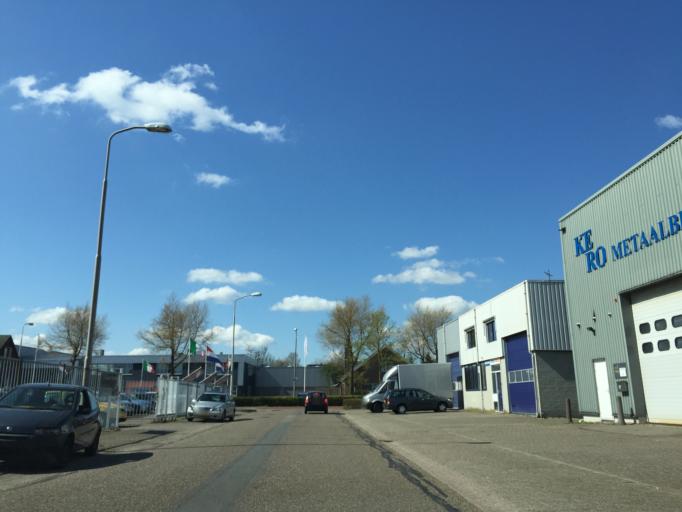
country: NL
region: South Holland
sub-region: Gemeente Pijnacker-Nootdorp
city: Pijnacker
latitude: 52.0272
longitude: 4.4375
